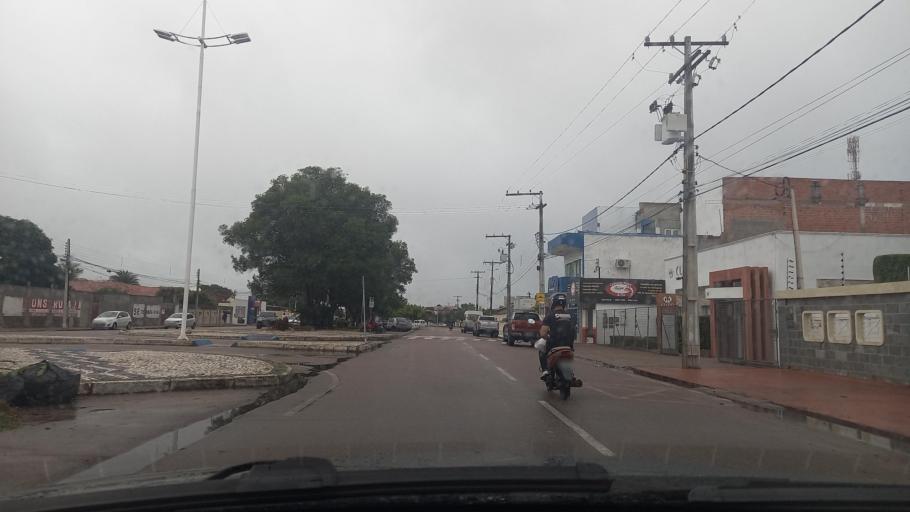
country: BR
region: Bahia
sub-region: Paulo Afonso
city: Paulo Afonso
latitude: -9.4044
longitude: -38.2266
